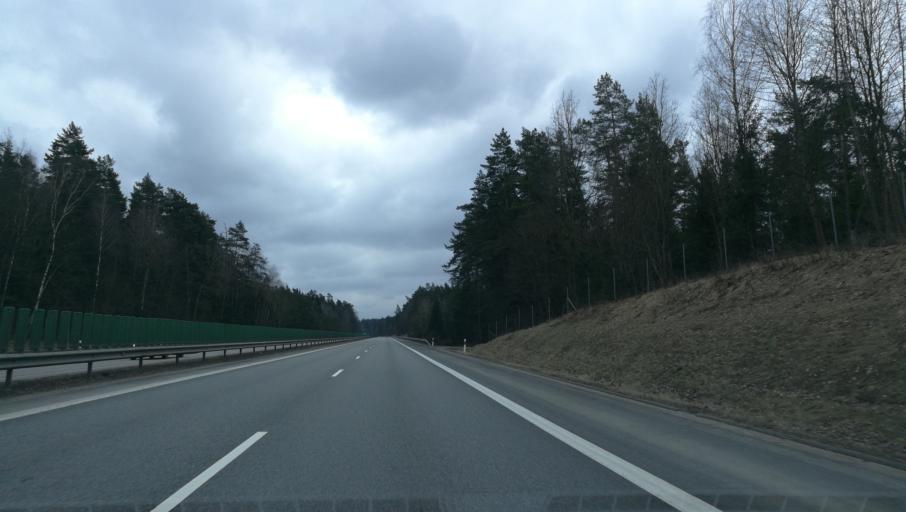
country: LT
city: Trakai
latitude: 54.7276
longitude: 24.9613
